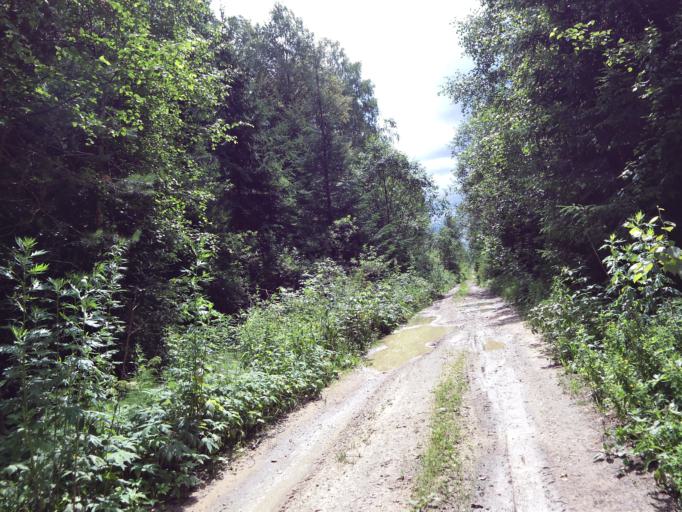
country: RU
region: Moskovskaya
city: Popovo
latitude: 54.9766
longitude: 37.6951
